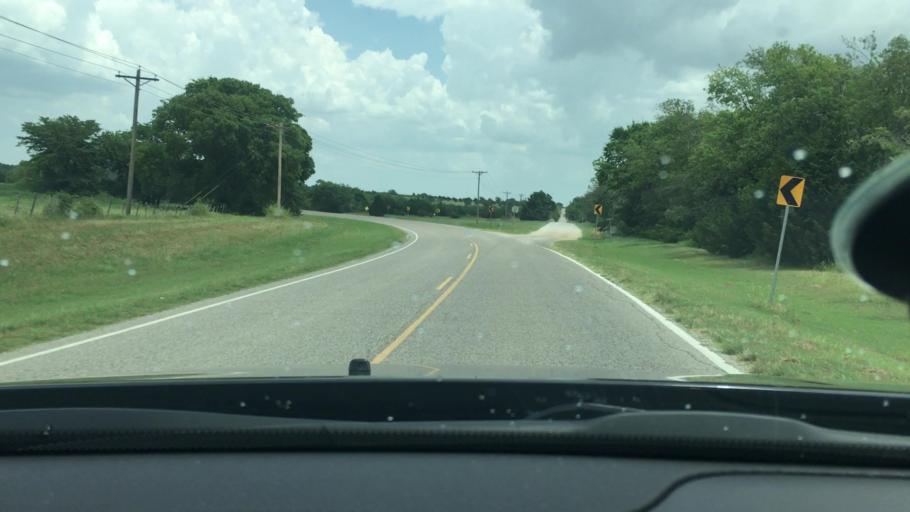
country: US
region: Oklahoma
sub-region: Love County
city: Marietta
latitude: 33.9403
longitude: -97.0430
